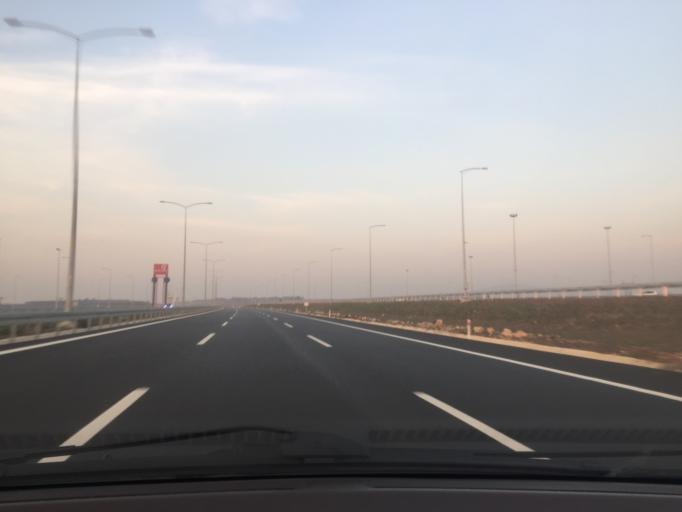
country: TR
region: Bursa
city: Karacabey
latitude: 40.2517
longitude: 28.4522
